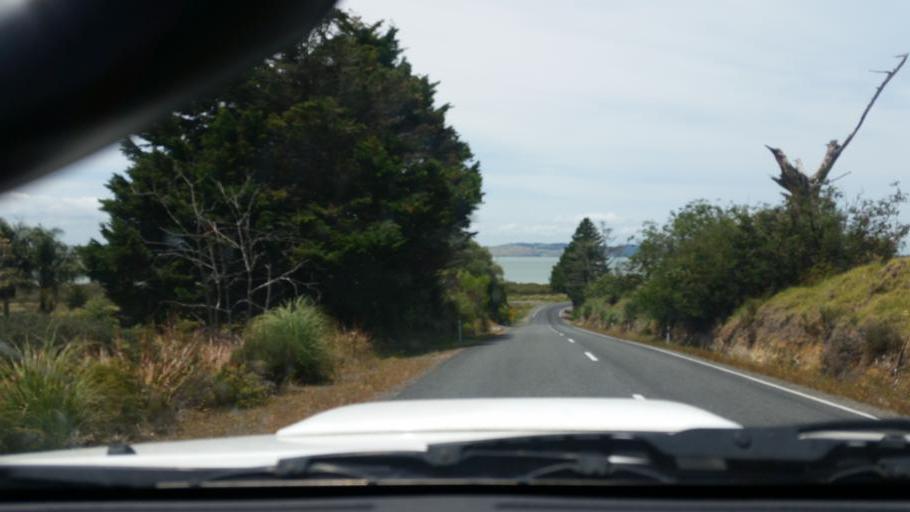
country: NZ
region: Northland
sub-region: Kaipara District
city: Dargaville
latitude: -36.1751
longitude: 174.0247
